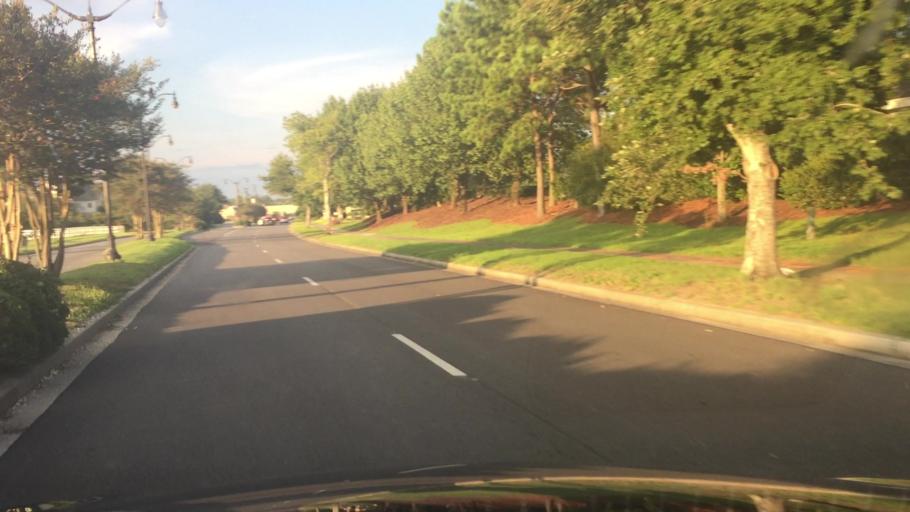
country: US
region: South Carolina
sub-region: Horry County
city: Forestbrook
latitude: 33.7113
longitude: -78.9313
